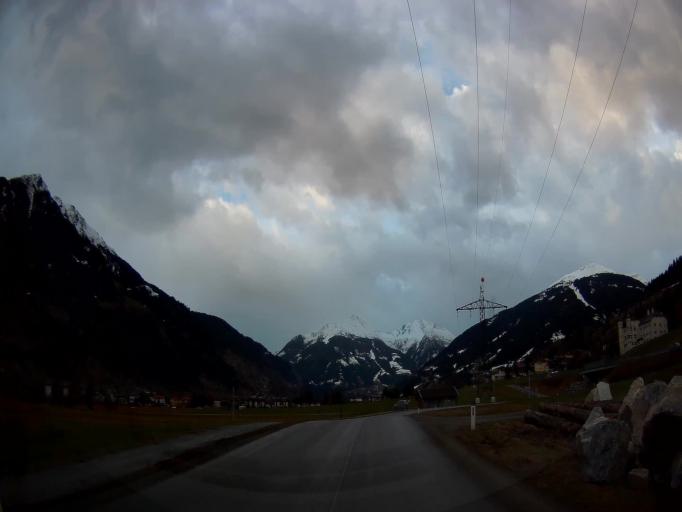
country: AT
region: Salzburg
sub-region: Politischer Bezirk Sankt Johann im Pongau
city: Bad Hofgastein
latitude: 47.1648
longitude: 13.1000
